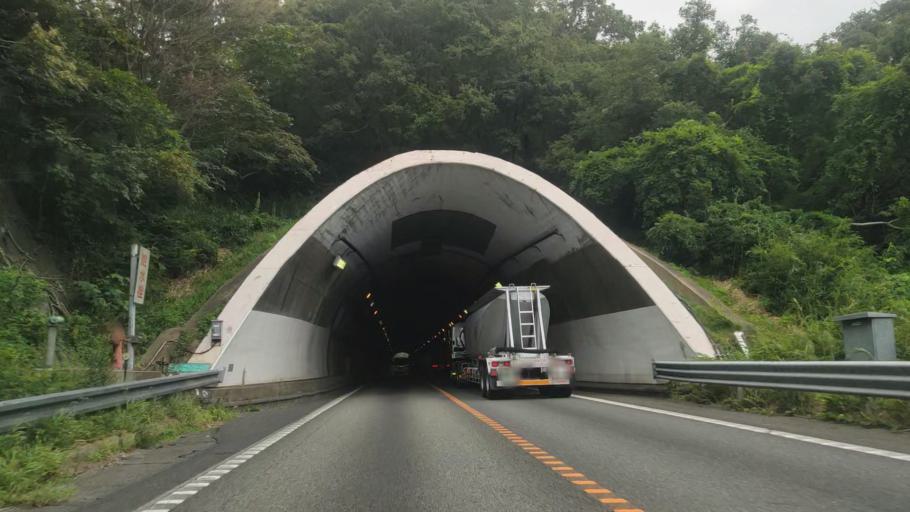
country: JP
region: Osaka
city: Kashihara
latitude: 34.5564
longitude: 135.6549
